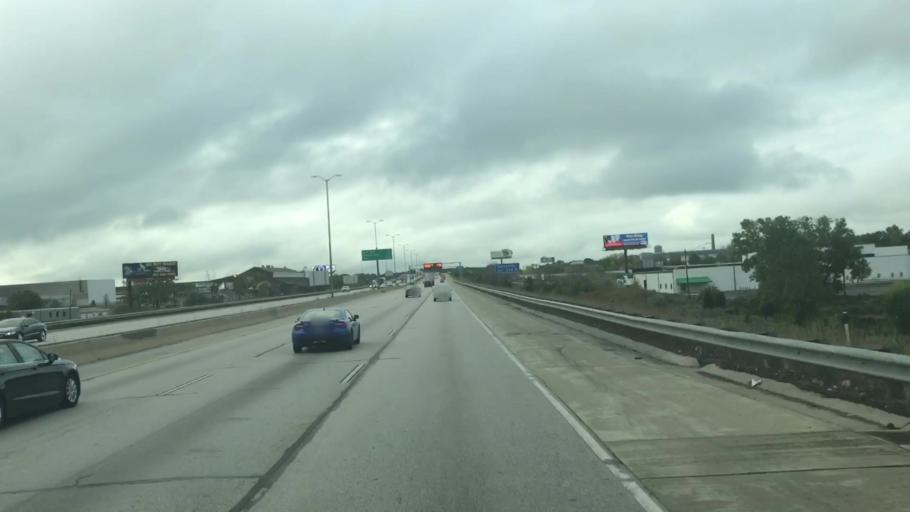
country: US
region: Wisconsin
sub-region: Milwaukee County
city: Milwaukee
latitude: 42.9947
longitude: -87.9152
